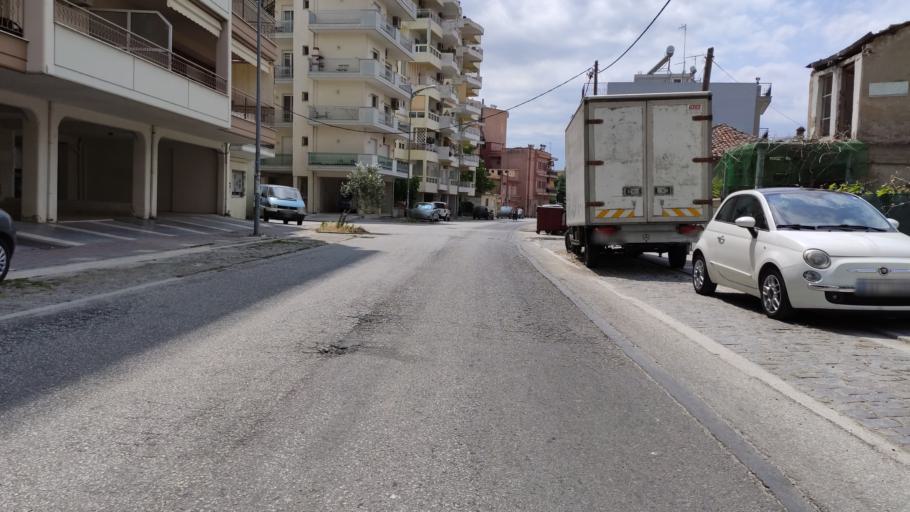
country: GR
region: East Macedonia and Thrace
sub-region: Nomos Rodopis
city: Komotini
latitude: 41.1224
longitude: 25.4001
